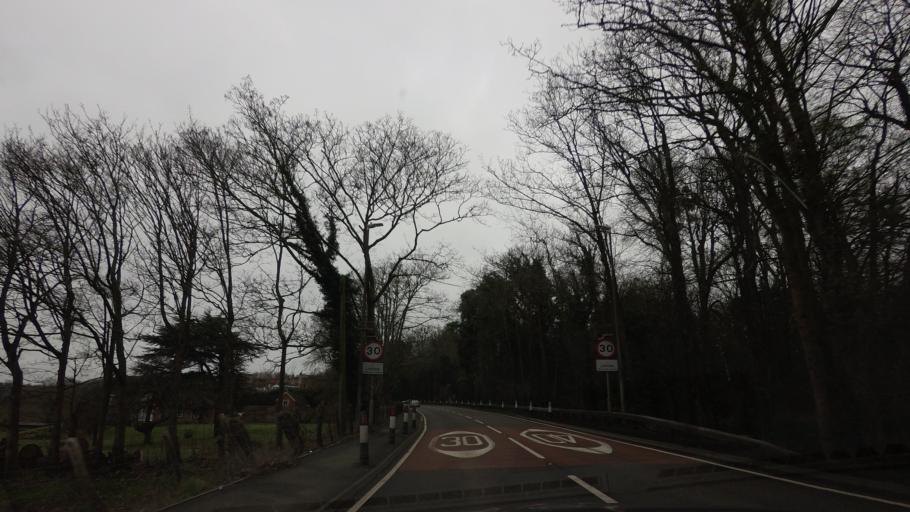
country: GB
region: England
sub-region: Kent
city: Maidstone
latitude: 51.2214
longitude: 0.5113
